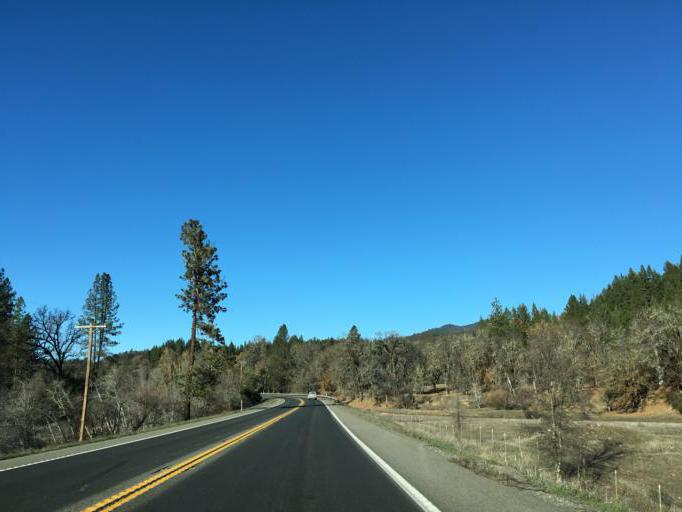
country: US
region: California
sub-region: Mendocino County
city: Laytonville
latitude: 39.7361
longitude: -123.5138
